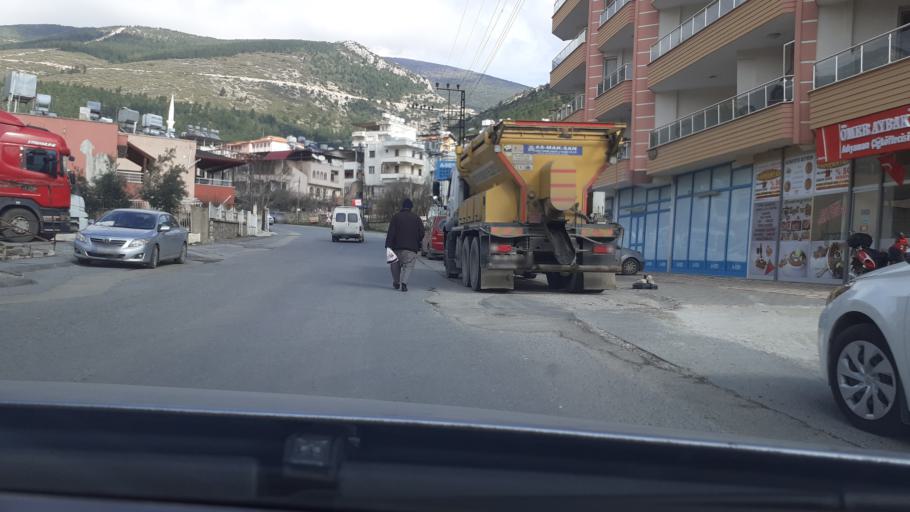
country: TR
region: Hatay
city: Belen
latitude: 36.4891
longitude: 36.2247
